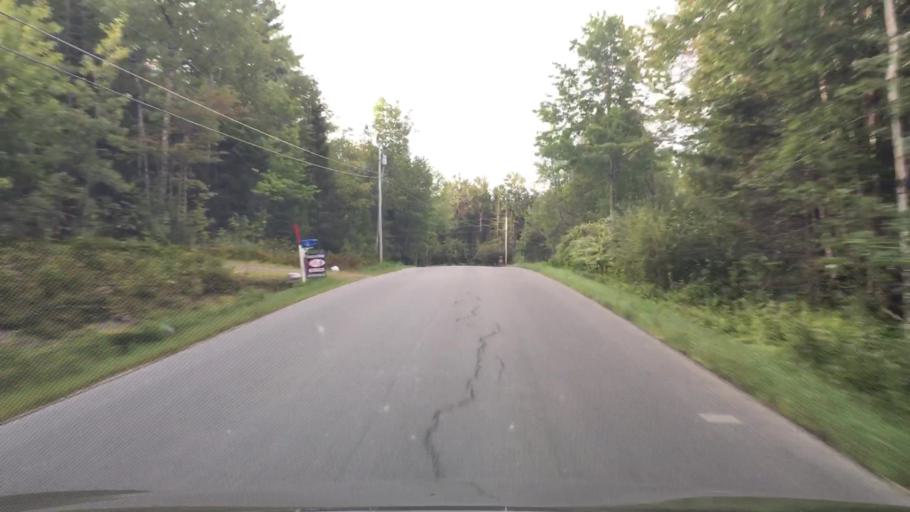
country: US
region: Maine
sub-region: Waldo County
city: Stockton Springs
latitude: 44.4956
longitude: -68.8741
